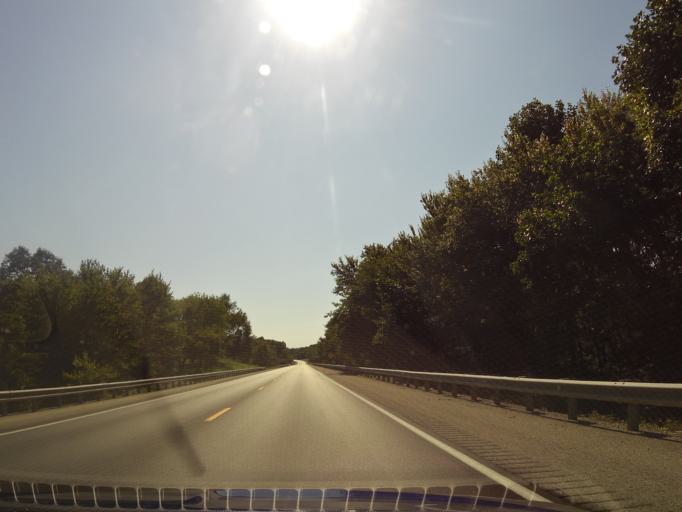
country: US
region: Kentucky
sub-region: Laurel County
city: London
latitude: 37.1116
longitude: -84.0033
